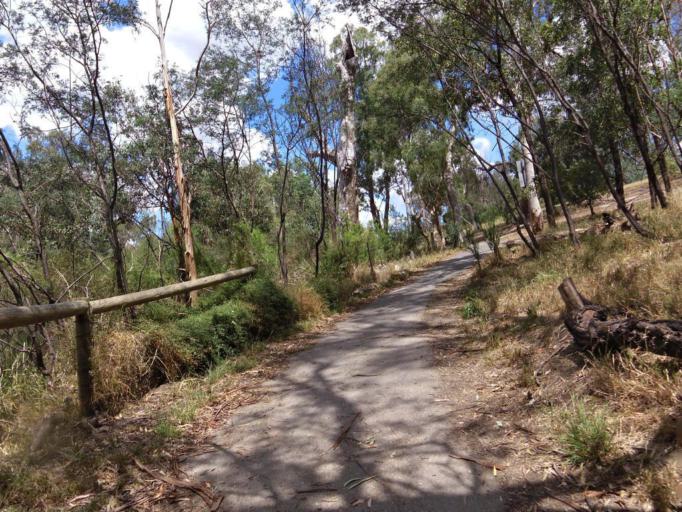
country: AU
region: Victoria
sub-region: Nillumbik
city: Eltham
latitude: -37.7362
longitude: 145.1450
